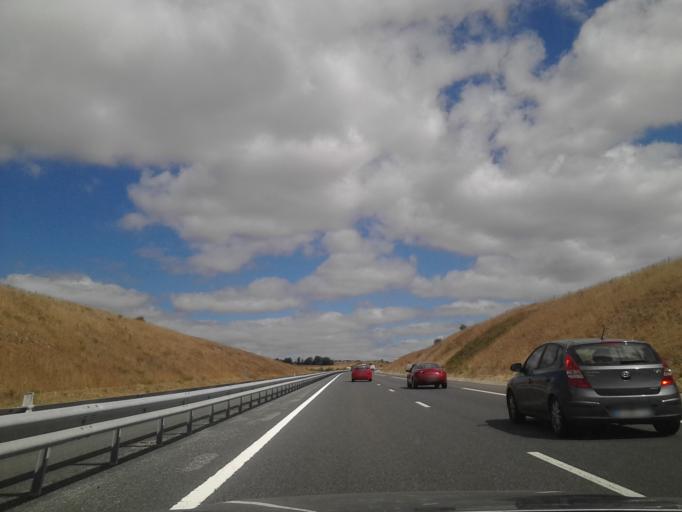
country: FR
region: Midi-Pyrenees
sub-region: Departement de l'Aveyron
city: Creissels
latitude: 44.1142
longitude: 3.0297
